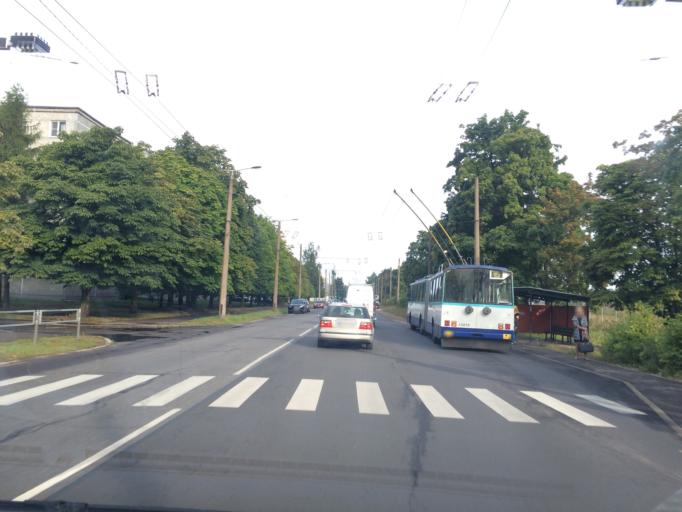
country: LV
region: Kekava
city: Kekava
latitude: 56.9028
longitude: 24.2138
